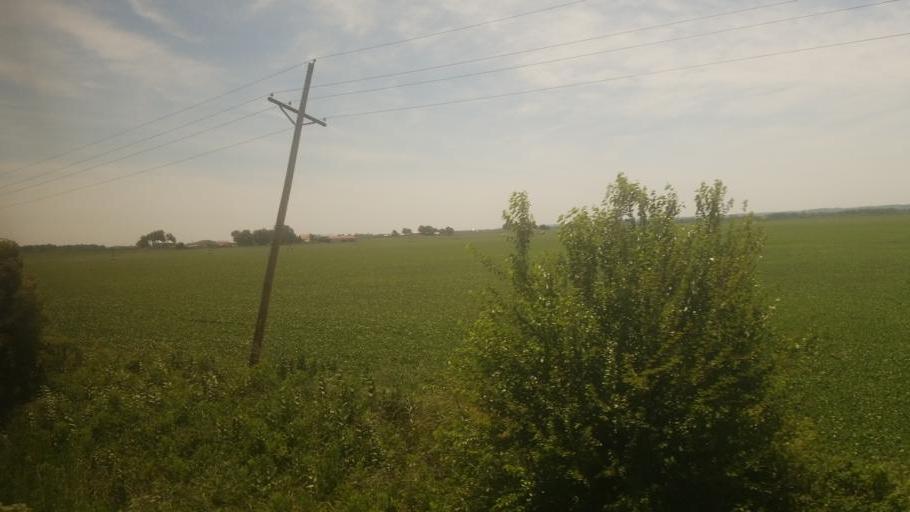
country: US
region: Missouri
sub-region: Carroll County
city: Carrollton
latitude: 39.2986
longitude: -93.6999
